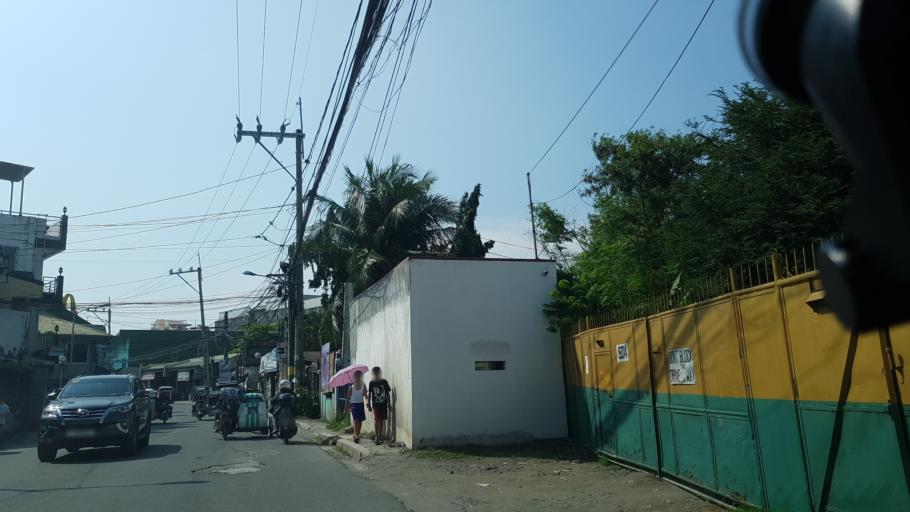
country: PH
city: Sambayanihan People's Village
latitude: 14.4913
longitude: 121.0166
